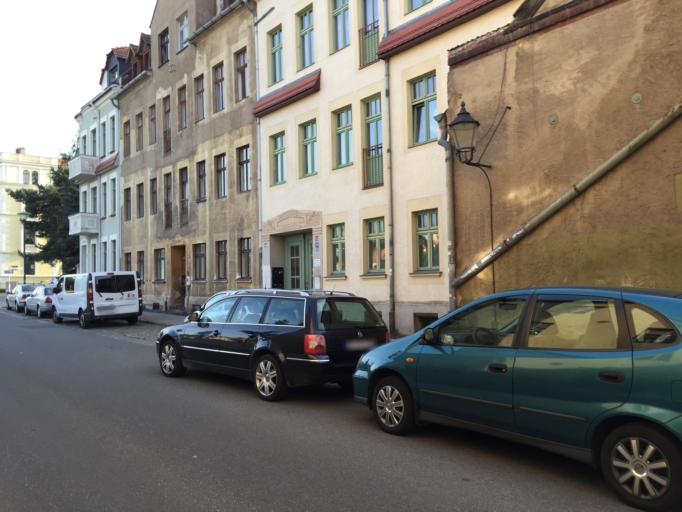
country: DE
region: Saxony
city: Goerlitz
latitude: 51.1551
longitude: 14.9959
